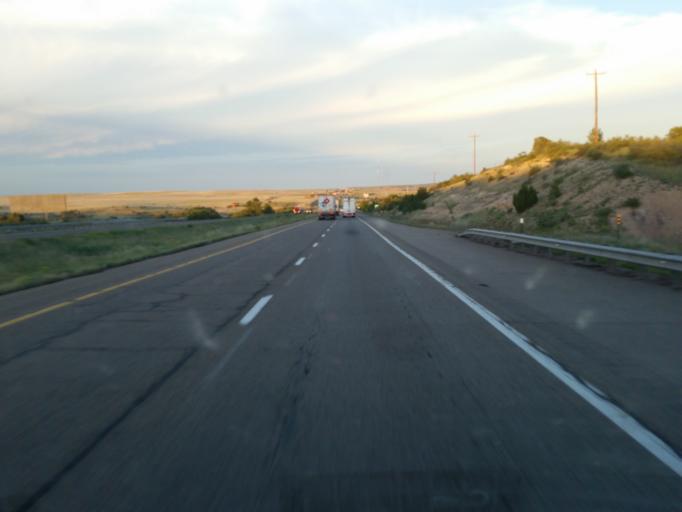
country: US
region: New Mexico
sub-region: San Miguel County
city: Las Vegas
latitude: 34.9925
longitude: -105.3178
